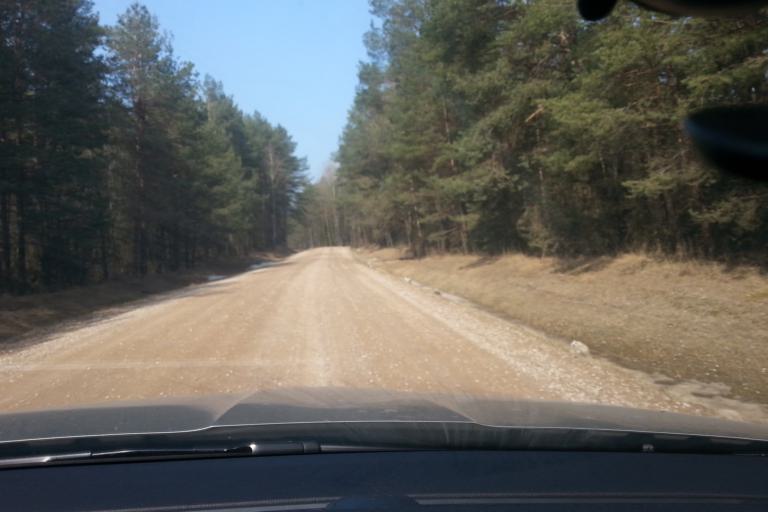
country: LT
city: Trakai
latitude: 54.5622
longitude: 24.9778
